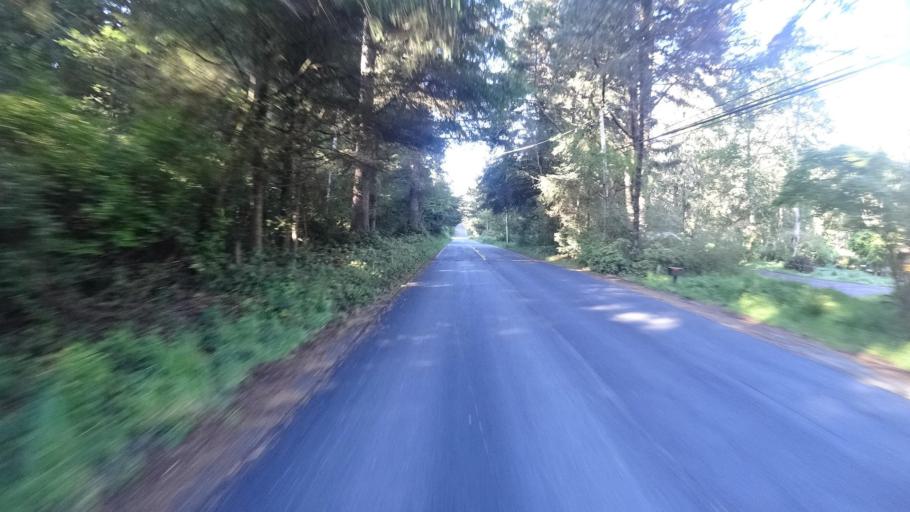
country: US
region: California
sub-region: Humboldt County
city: Westhaven-Moonstone
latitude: 41.1291
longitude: -124.1548
